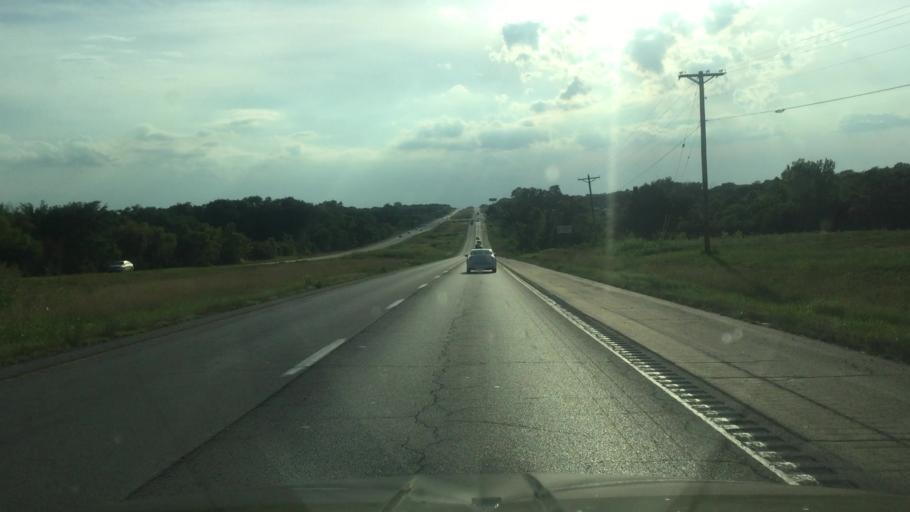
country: US
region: Missouri
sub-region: Jackson County
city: Lone Jack
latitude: 38.8701
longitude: -94.1220
